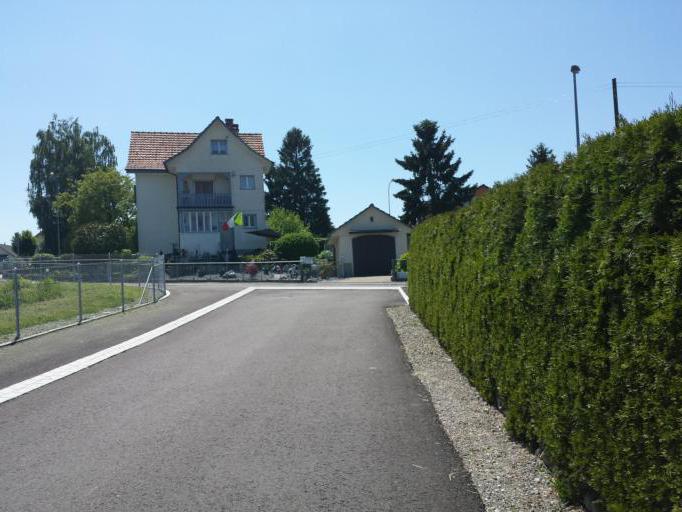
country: CH
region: Thurgau
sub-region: Arbon District
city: Uttwil
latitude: 47.5815
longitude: 9.3476
